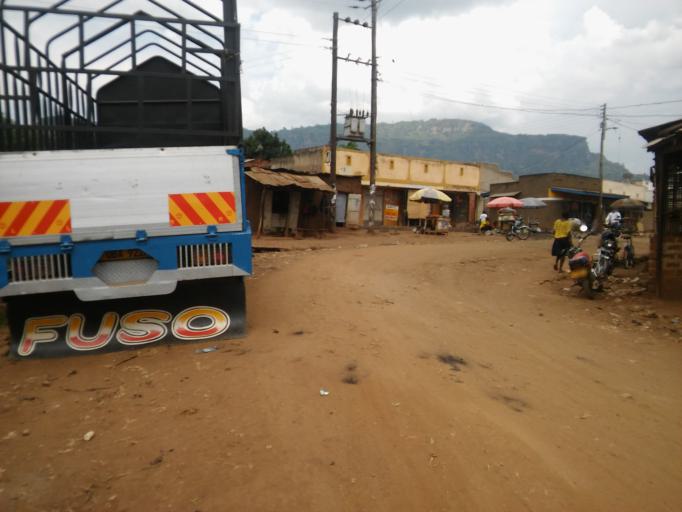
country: UG
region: Eastern Region
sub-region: Mbale District
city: Mbale
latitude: 1.0614
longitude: 34.2013
